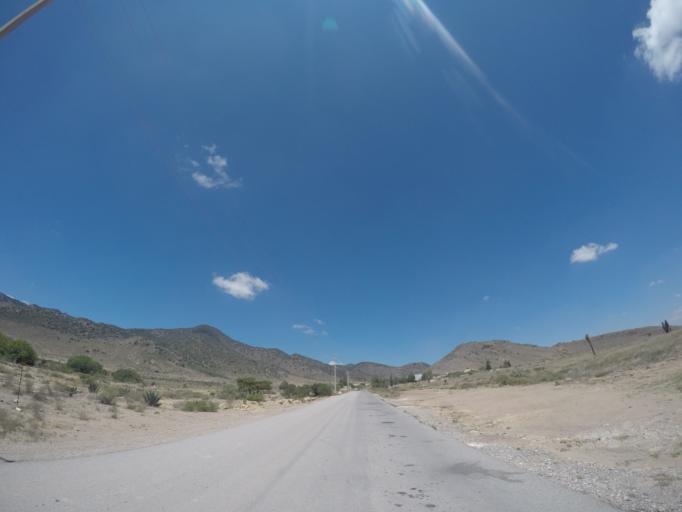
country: MX
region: San Luis Potosi
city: La Pila
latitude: 22.0152
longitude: -100.9142
